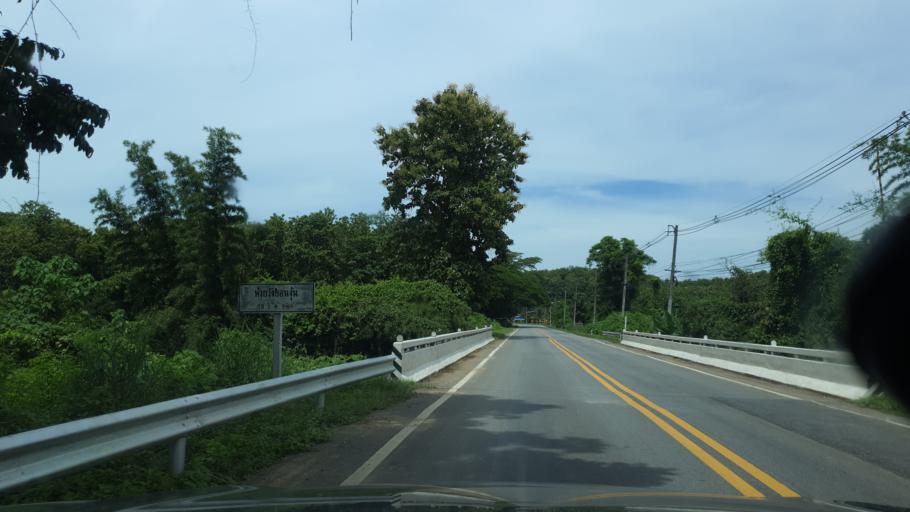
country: TH
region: Sukhothai
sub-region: Amphoe Si Satchanalai
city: Si Satchanalai
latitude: 17.6291
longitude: 99.7000
